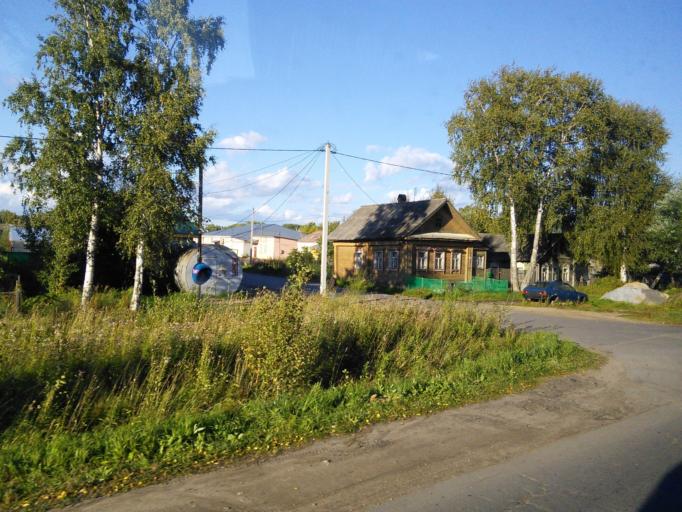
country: RU
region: Jaroslavl
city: Poshekhon'ye
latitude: 58.4980
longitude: 39.1162
